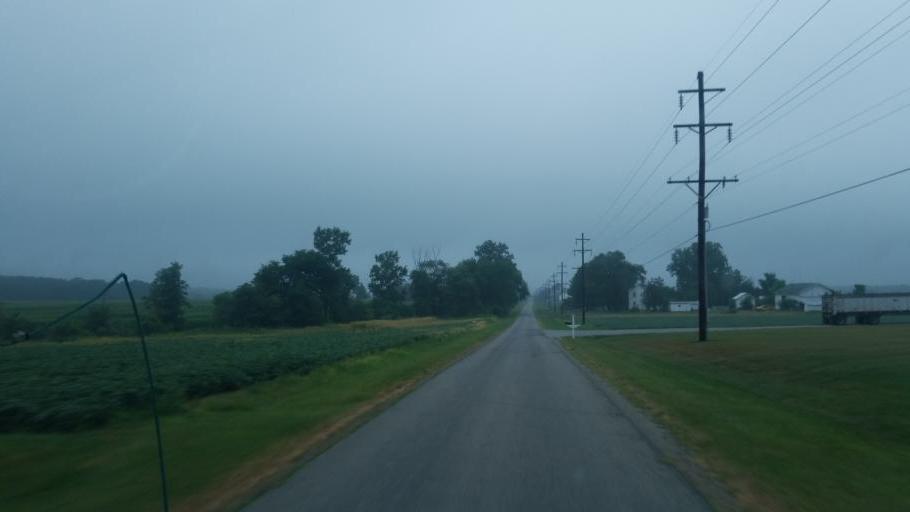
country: US
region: Ohio
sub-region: Defiance County
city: Hicksville
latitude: 41.3539
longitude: -84.7237
